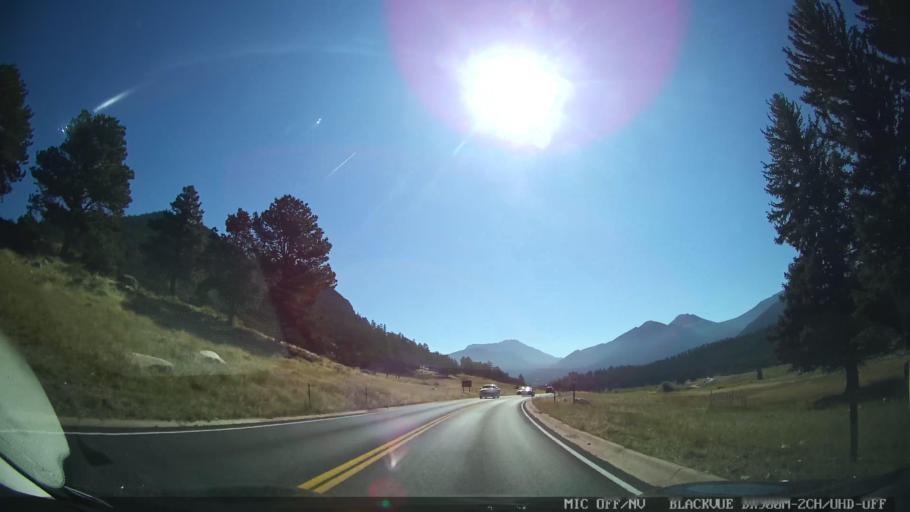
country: US
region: Colorado
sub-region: Larimer County
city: Estes Park
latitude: 40.3578
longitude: -105.5855
